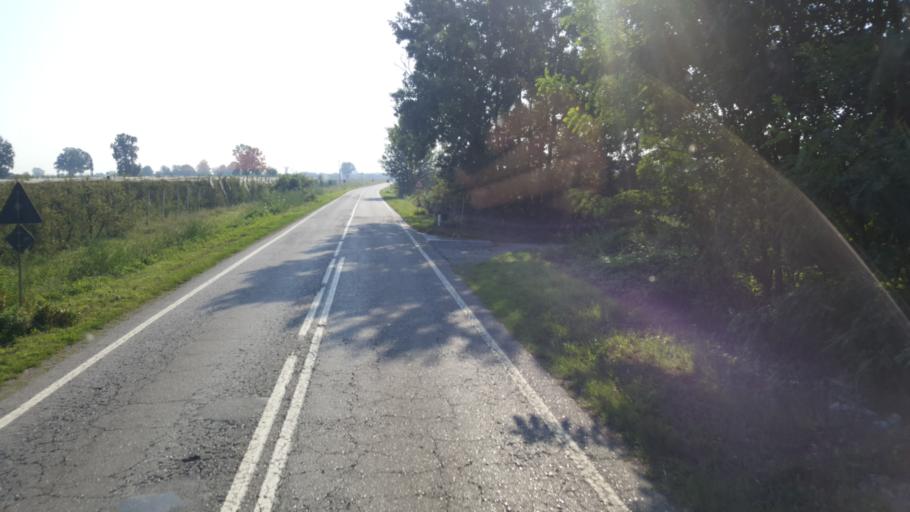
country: IT
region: Lombardy
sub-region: Provincia di Cremona
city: Robecco d'Oglio
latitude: 45.2628
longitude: 10.0466
